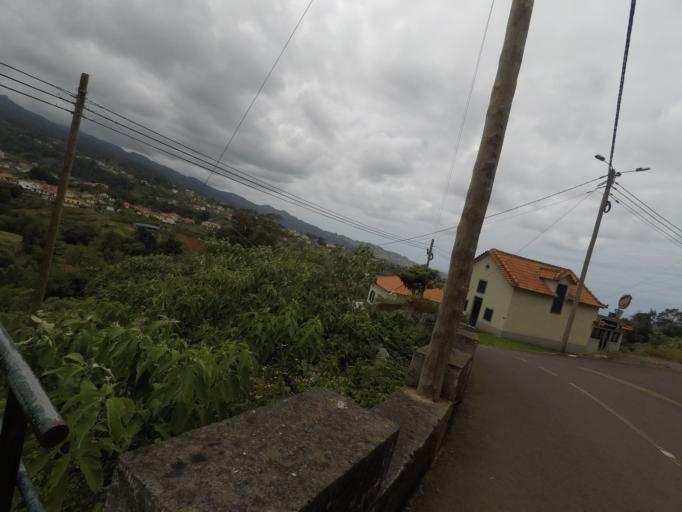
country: PT
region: Madeira
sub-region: Santana
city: Santana
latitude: 32.7972
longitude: -16.8667
